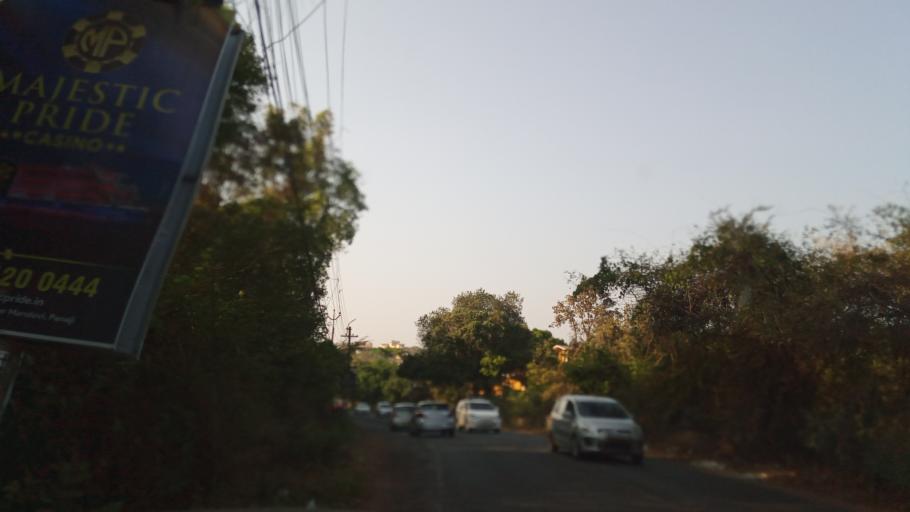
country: IN
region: Goa
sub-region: North Goa
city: Serula
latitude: 15.5418
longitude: 73.8165
